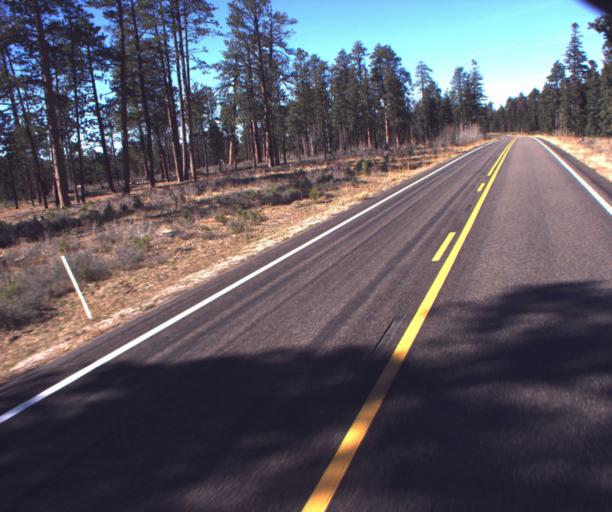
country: US
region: Arizona
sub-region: Coconino County
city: Fredonia
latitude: 36.6418
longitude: -112.1750
